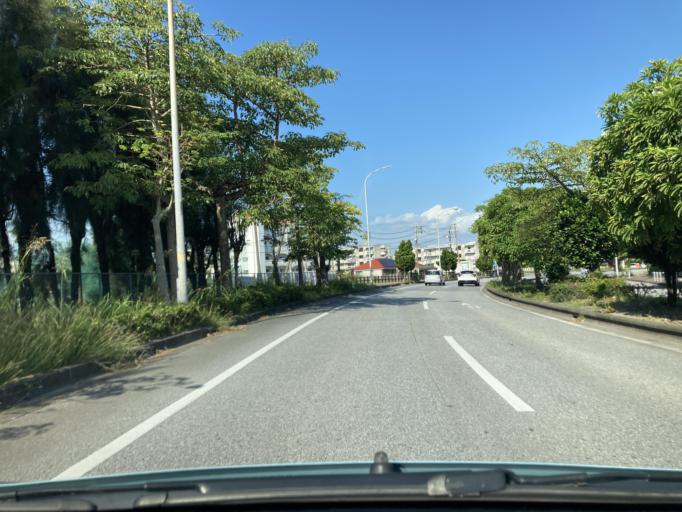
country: JP
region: Okinawa
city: Okinawa
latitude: 26.3056
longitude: 127.8161
